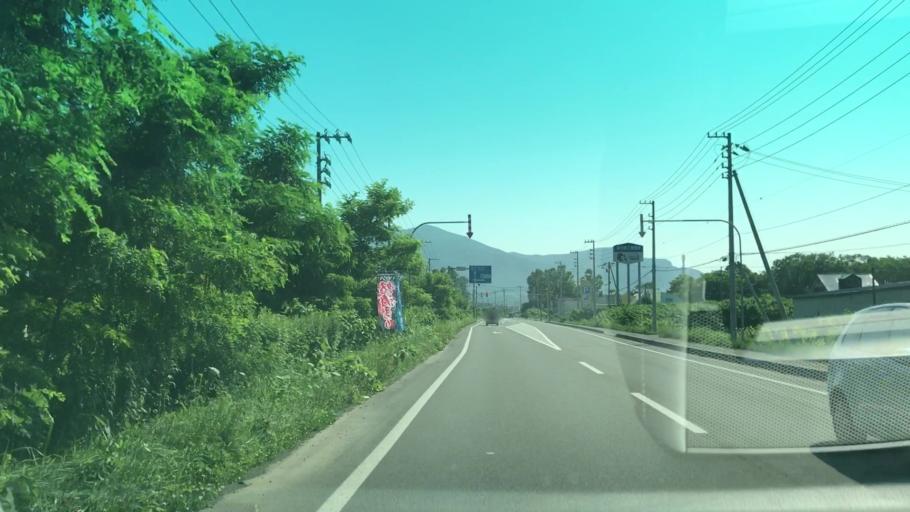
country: JP
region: Hokkaido
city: Iwanai
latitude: 42.9940
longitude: 140.5336
